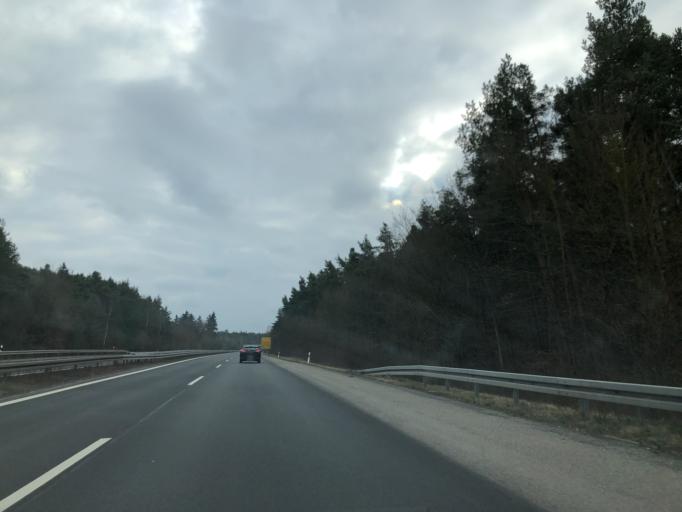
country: DE
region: Bavaria
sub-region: Regierungsbezirk Mittelfranken
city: Rednitzhembach
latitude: 49.3037
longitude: 11.0866
